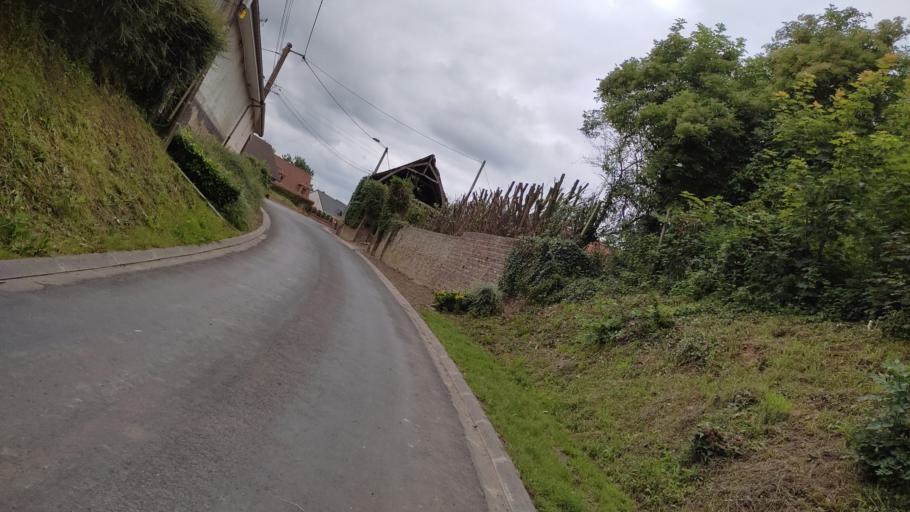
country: FR
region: Nord-Pas-de-Calais
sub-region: Departement du Pas-de-Calais
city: Beaumetz-les-Loges
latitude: 50.2580
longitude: 2.6494
